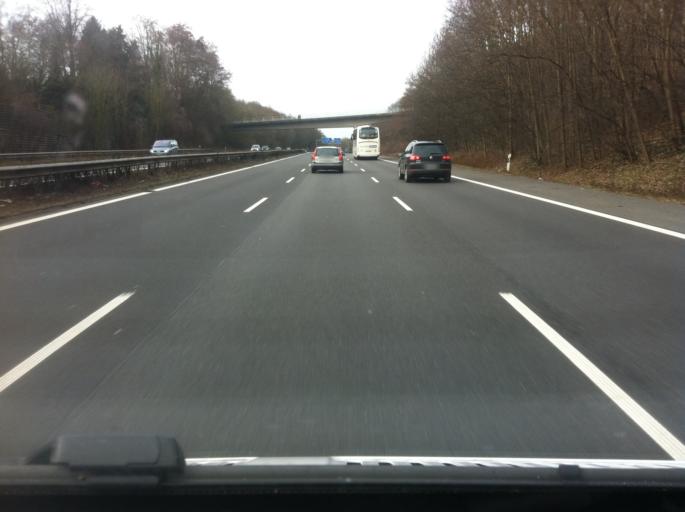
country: DE
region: North Rhine-Westphalia
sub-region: Regierungsbezirk Koln
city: Konigswinter
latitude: 50.7173
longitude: 7.1708
